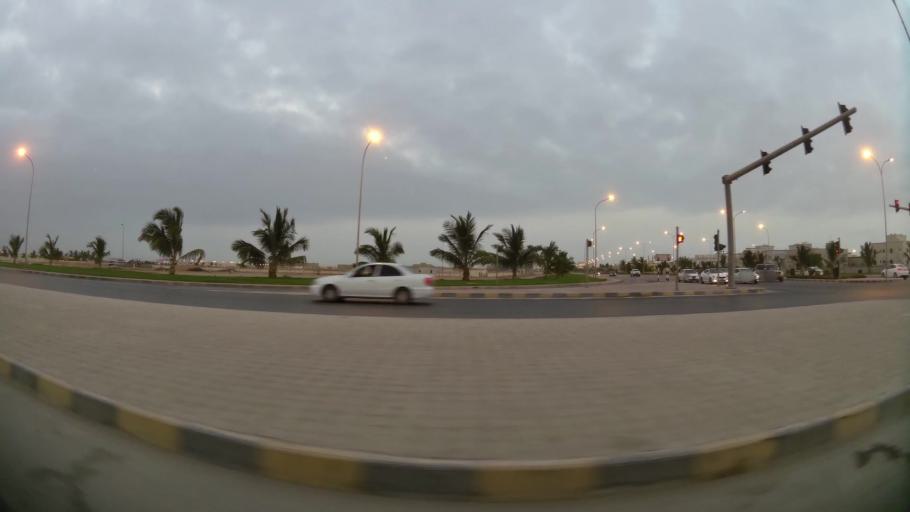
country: OM
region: Zufar
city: Salalah
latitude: 17.0207
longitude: 54.0343
